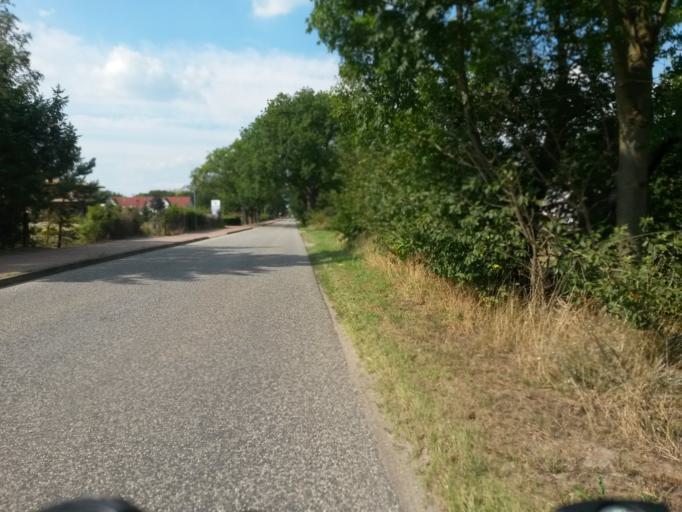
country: DE
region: Brandenburg
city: Templin
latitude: 53.1044
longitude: 13.5258
